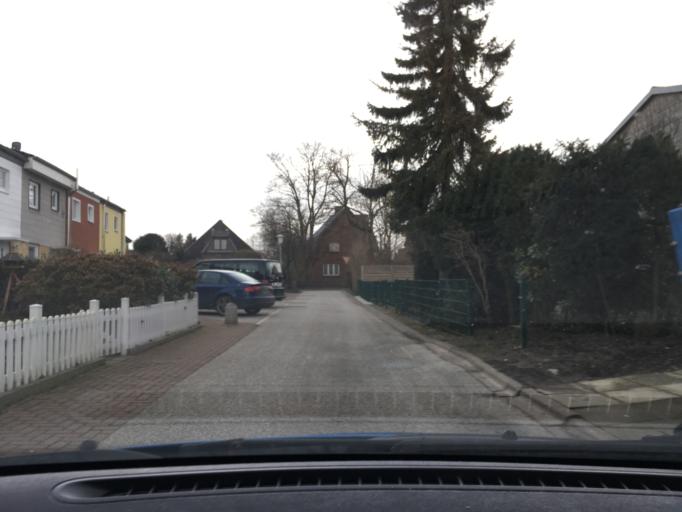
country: DE
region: Schleswig-Holstein
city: Wedel
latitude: 53.5795
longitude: 9.7189
